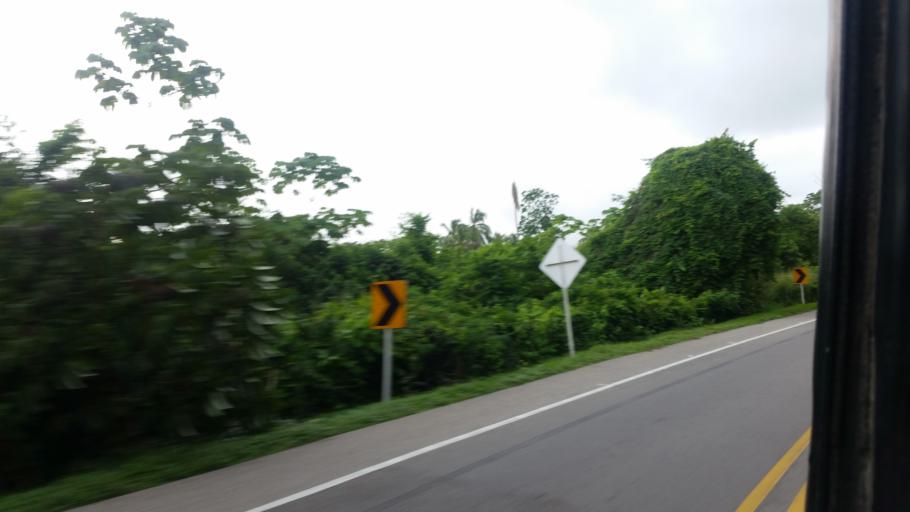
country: CO
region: Magdalena
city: Santa Marta
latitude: 11.2749
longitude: -73.8640
